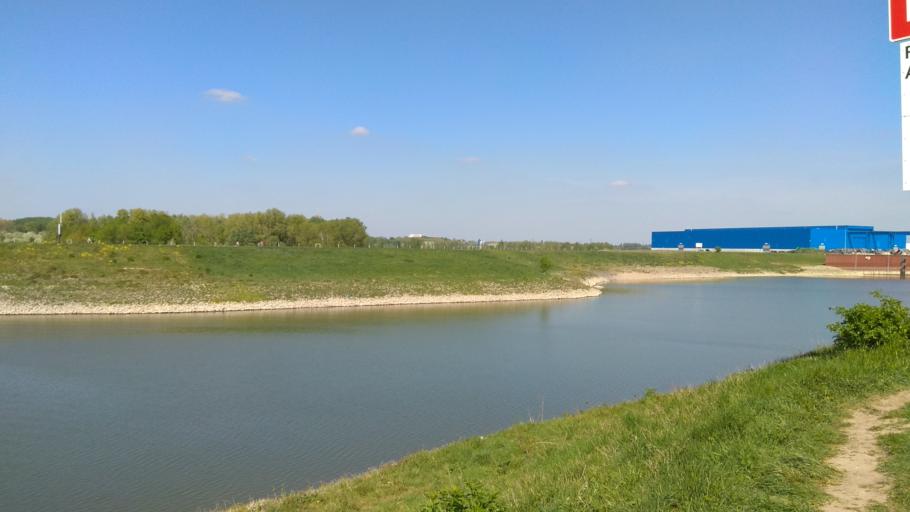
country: DE
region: North Rhine-Westphalia
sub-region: Regierungsbezirk Dusseldorf
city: Wesel
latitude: 51.6336
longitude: 6.6088
